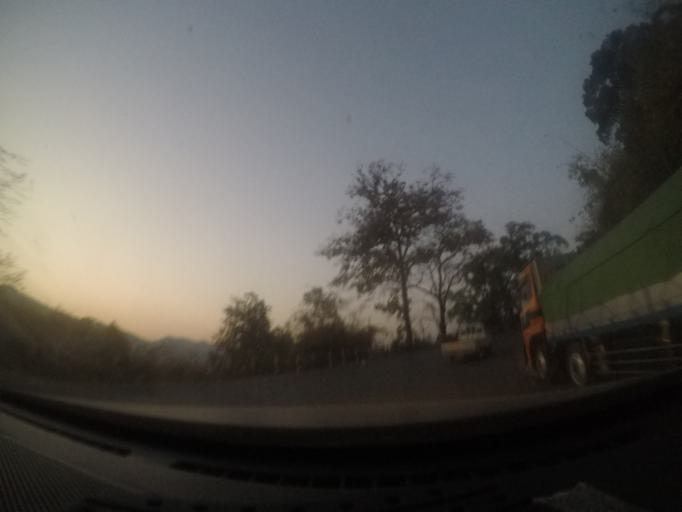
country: MM
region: Mandalay
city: Yamethin
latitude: 20.6946
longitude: 96.5065
